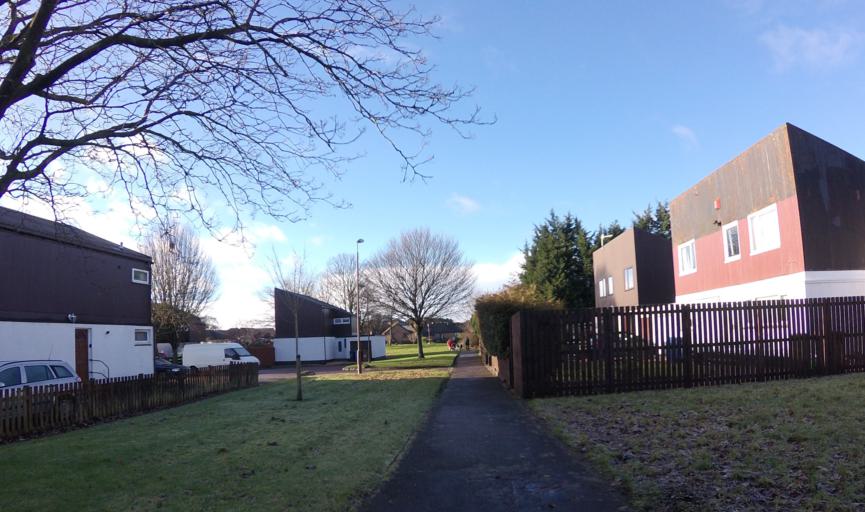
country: GB
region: Scotland
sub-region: West Lothian
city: Mid Calder
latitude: 55.8968
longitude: -3.4862
